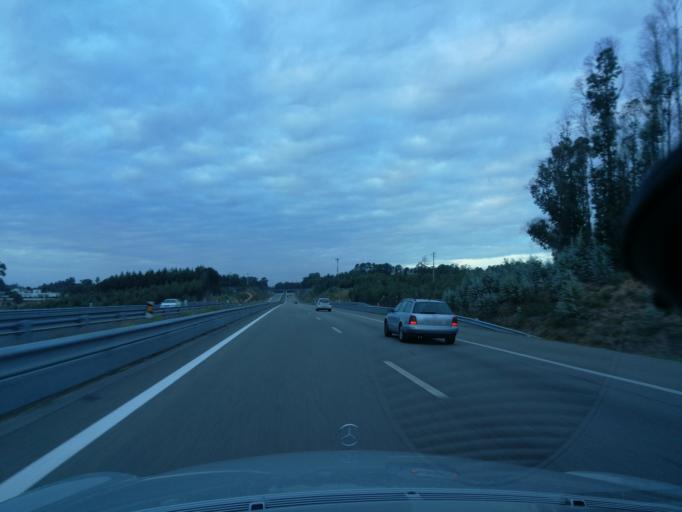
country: PT
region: Aveiro
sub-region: Estarreja
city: Salreu
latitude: 40.7119
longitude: -8.5328
